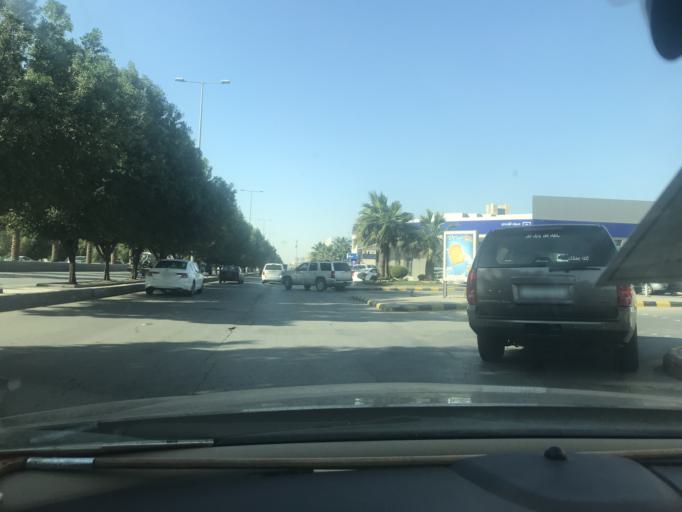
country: SA
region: Ar Riyad
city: Riyadh
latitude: 24.7511
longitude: 46.6706
